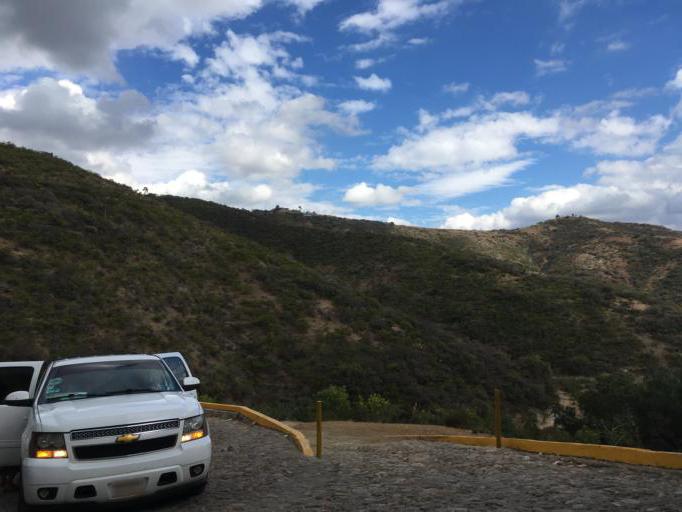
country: MX
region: Guanajuato
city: Guanajuato
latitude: 21.0433
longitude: -101.2581
